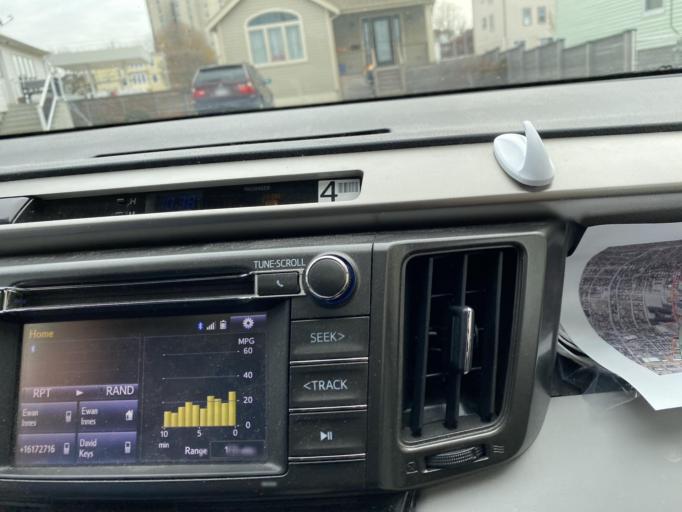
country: US
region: Massachusetts
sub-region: Bristol County
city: Fall River
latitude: 41.6859
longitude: -71.1312
